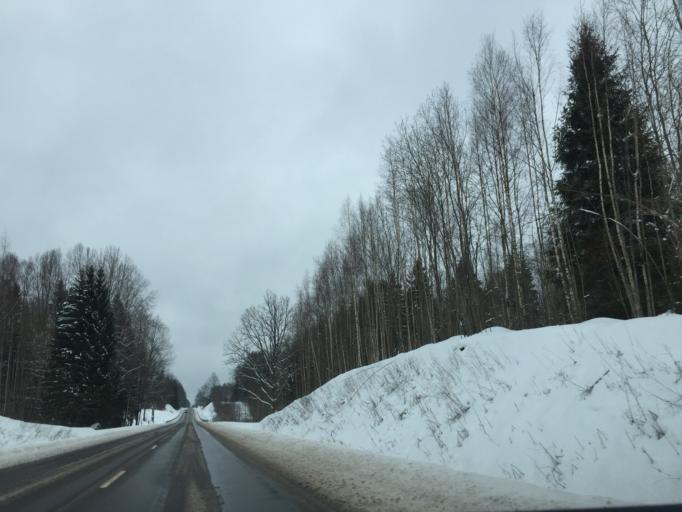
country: LV
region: Ligatne
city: Ligatne
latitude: 57.1335
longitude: 25.0852
